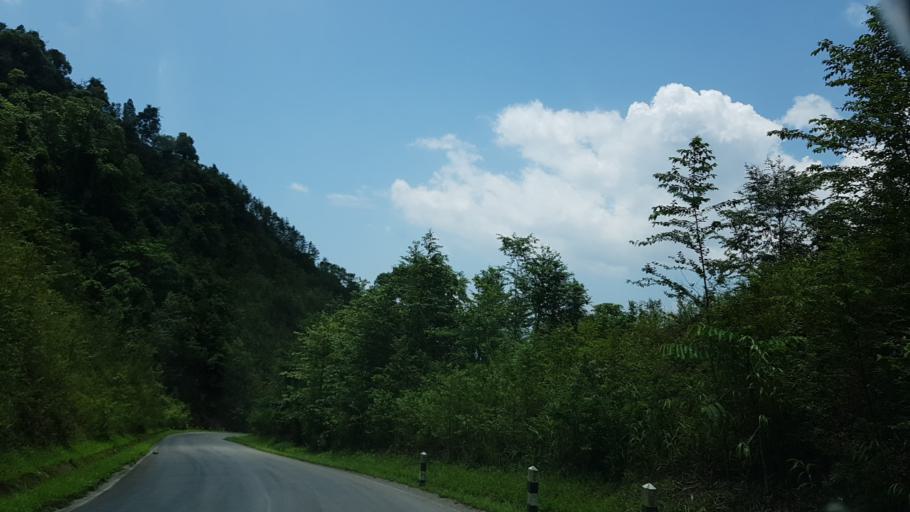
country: LA
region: Vientiane
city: Muang Kasi
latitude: 19.3749
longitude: 102.1580
